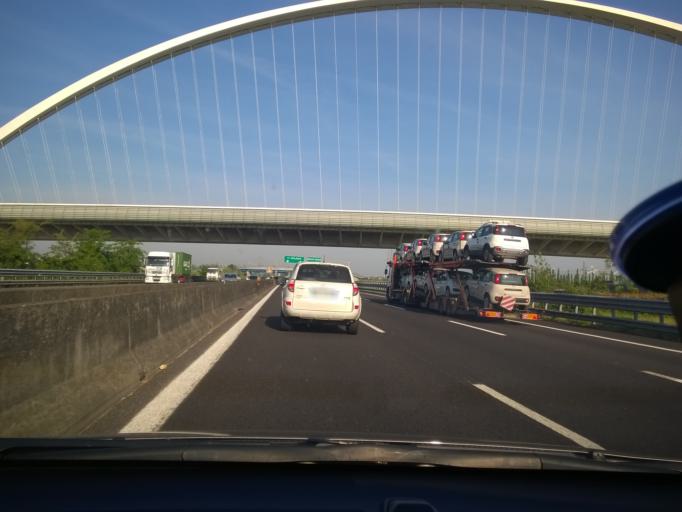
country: IT
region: Emilia-Romagna
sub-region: Provincia di Reggio Emilia
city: Reggio nell'Emilia
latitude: 44.7274
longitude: 10.6370
